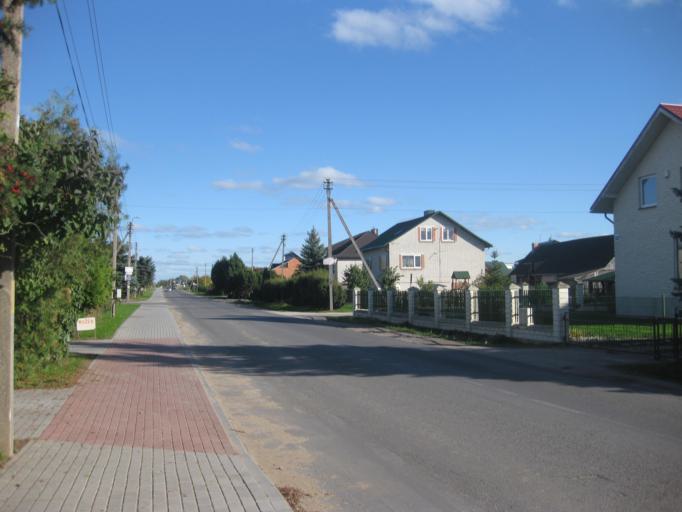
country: LT
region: Kauno apskritis
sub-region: Kauno rajonas
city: Garliava
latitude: 54.8389
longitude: 23.8818
